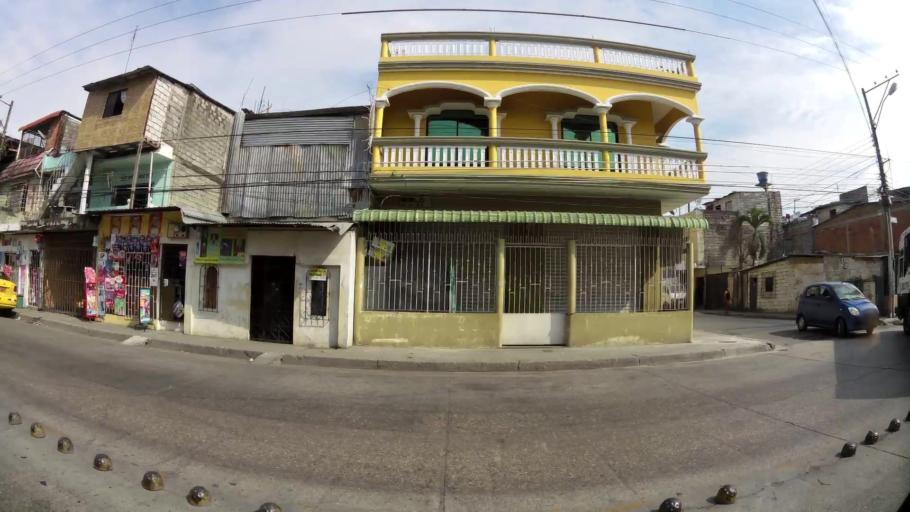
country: EC
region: Guayas
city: Guayaquil
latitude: -2.2550
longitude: -79.9021
